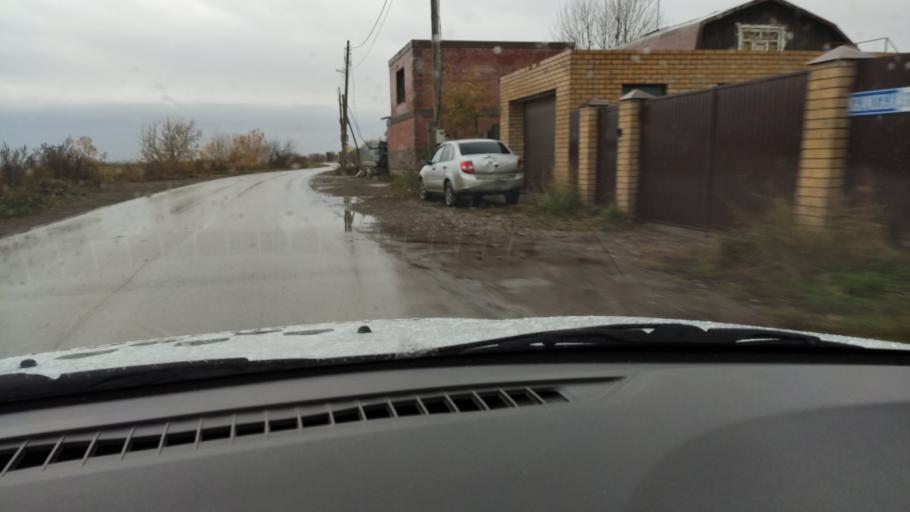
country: RU
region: Perm
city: Kondratovo
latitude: 57.9879
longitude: 56.0978
